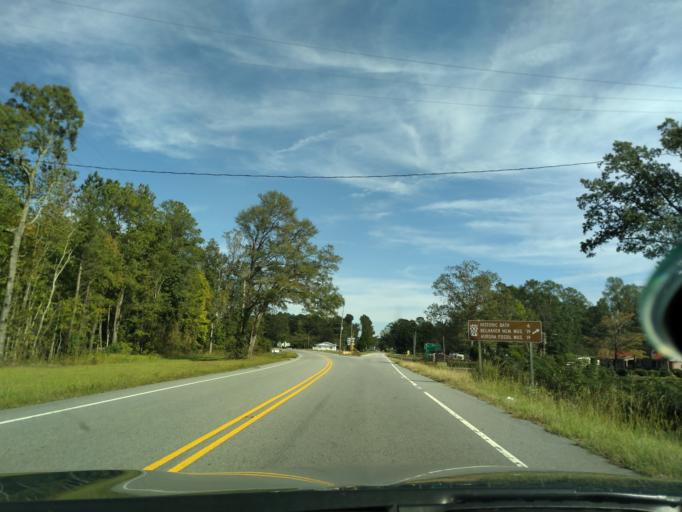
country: US
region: North Carolina
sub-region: Beaufort County
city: River Road
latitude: 35.5120
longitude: -76.9048
